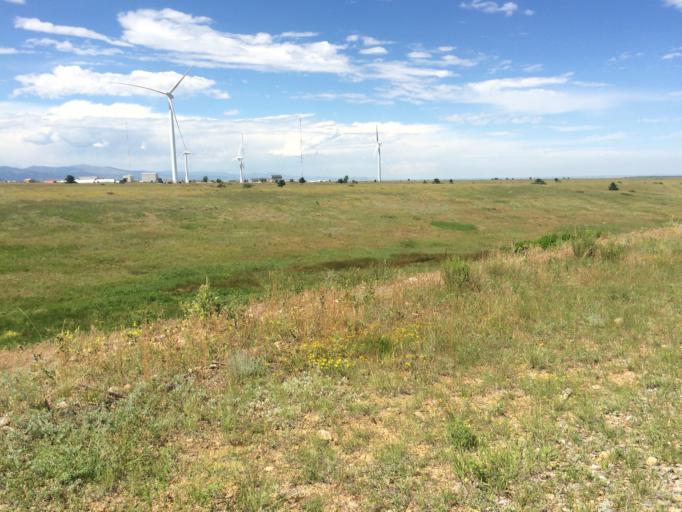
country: US
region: Colorado
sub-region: Boulder County
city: Superior
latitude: 39.9011
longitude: -105.2212
